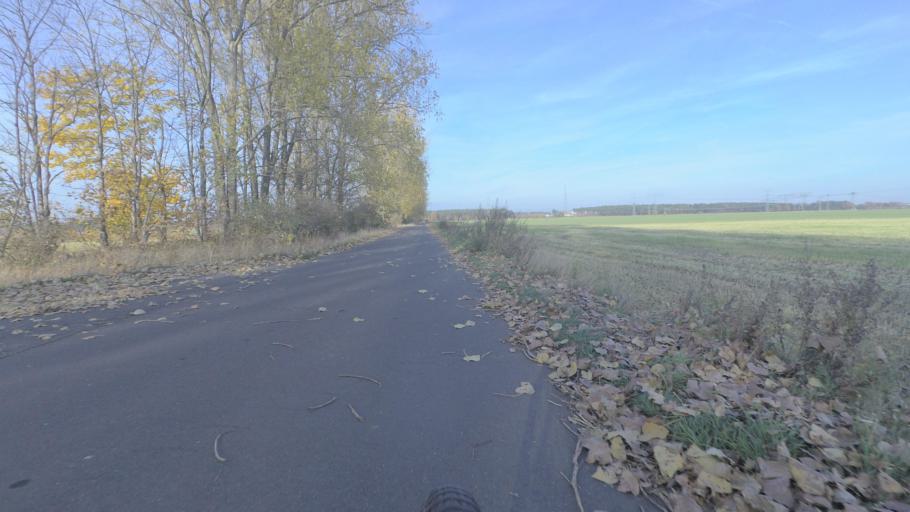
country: DE
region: Brandenburg
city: Trebbin
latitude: 52.2214
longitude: 13.2901
